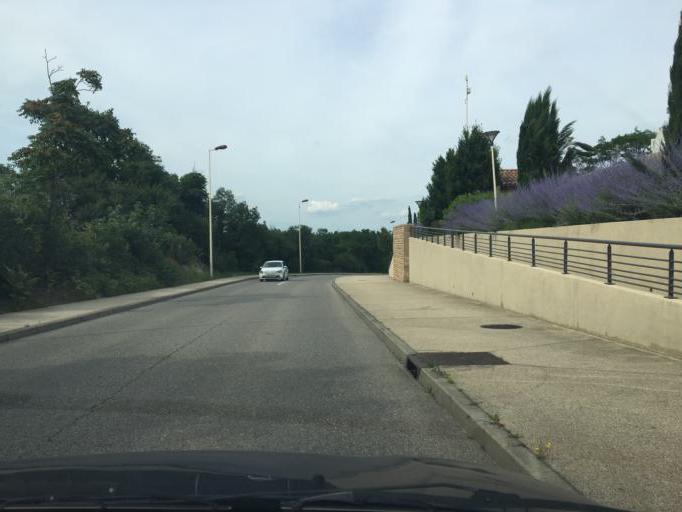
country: FR
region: Rhone-Alpes
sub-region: Departement de la Drome
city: Chateauneuf-sur-Isere
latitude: 45.0125
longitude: 4.9321
